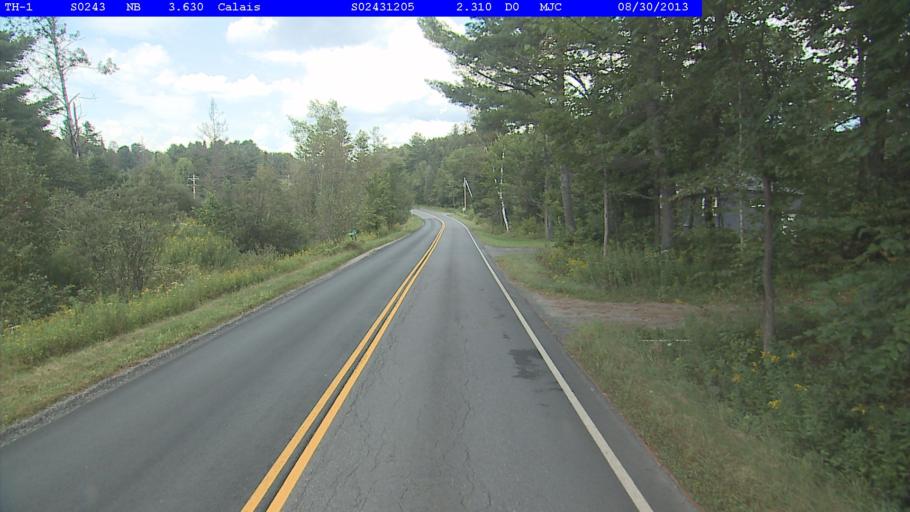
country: US
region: Vermont
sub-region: Washington County
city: Montpelier
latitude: 44.3646
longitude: -72.5031
